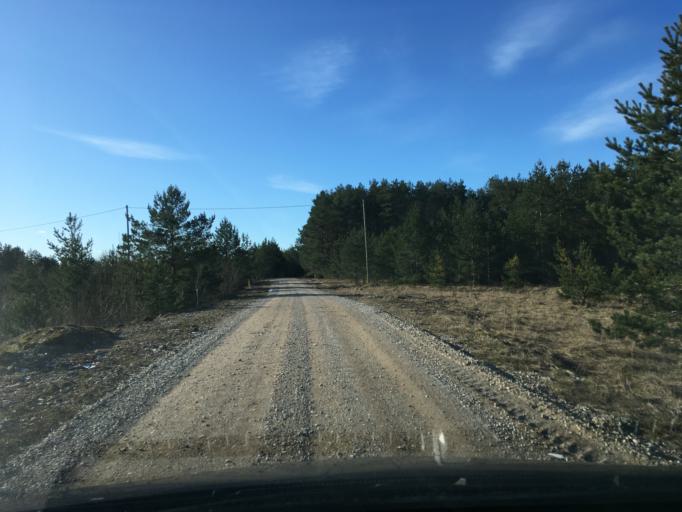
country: EE
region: Laeaene
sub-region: Lihula vald
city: Lihula
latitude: 58.5811
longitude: 23.7039
